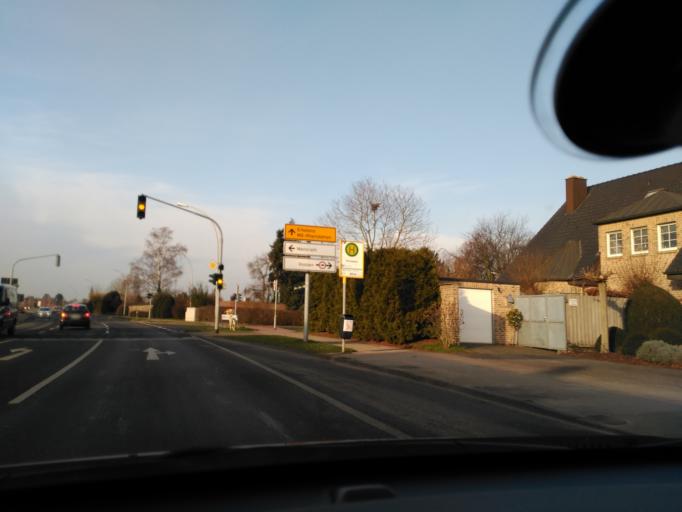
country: DE
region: North Rhine-Westphalia
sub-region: Regierungsbezirk Dusseldorf
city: Monchengladbach
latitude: 51.1497
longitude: 6.3807
